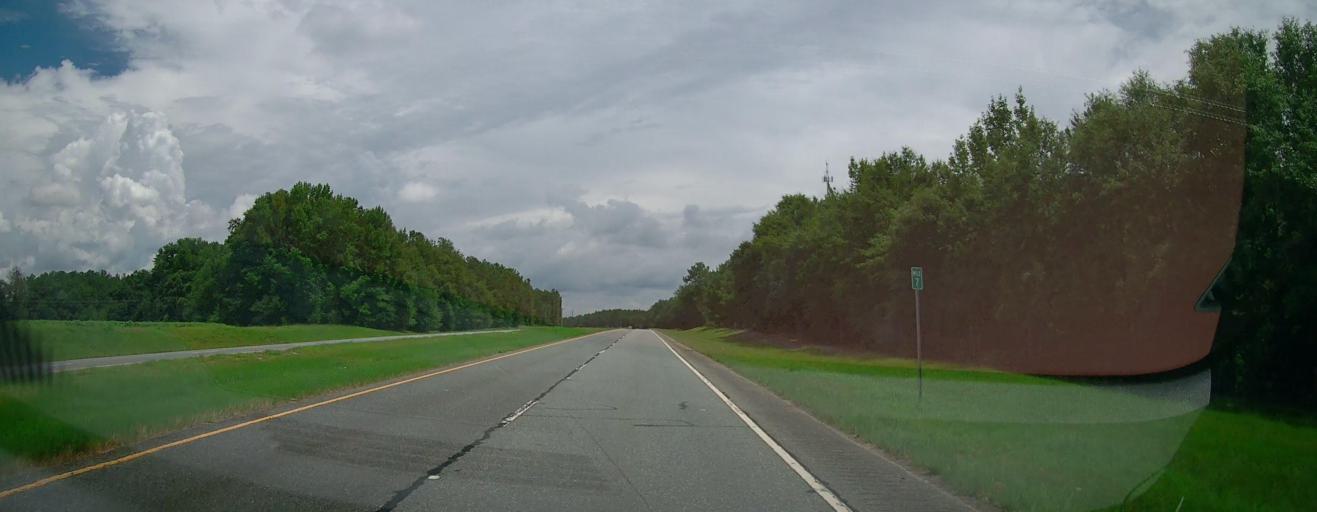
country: US
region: Georgia
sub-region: Dodge County
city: Eastman
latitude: 32.1913
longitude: -83.2056
